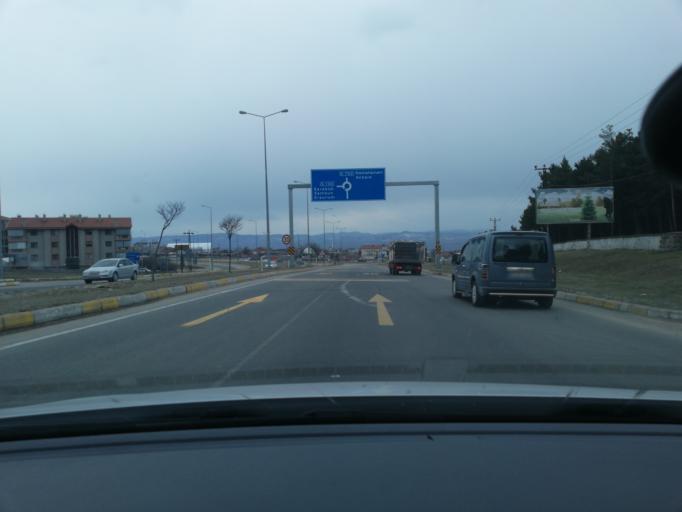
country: TR
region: Bolu
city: Gerede
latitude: 40.7931
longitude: 32.2067
